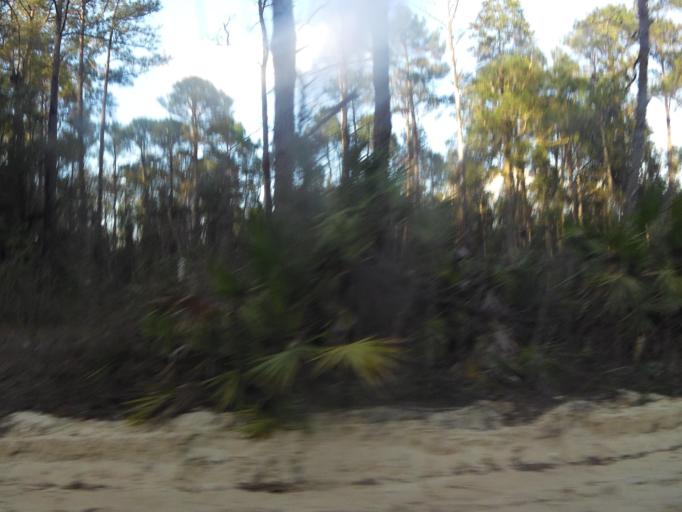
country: US
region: Florida
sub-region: Putnam County
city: Interlachen
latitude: 29.7835
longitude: -81.8635
